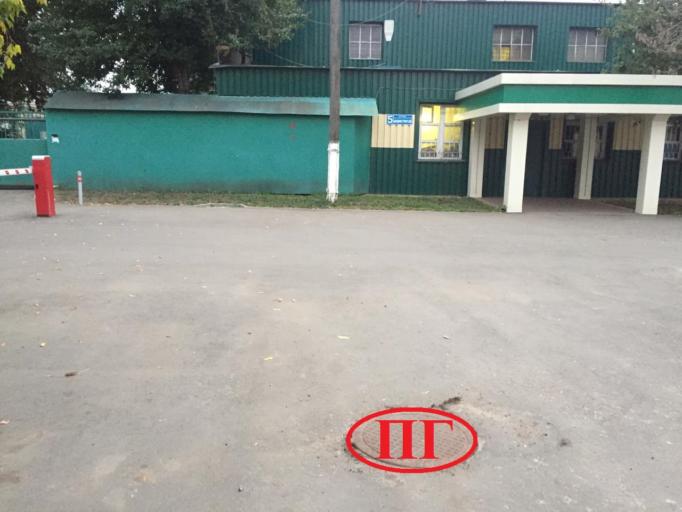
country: RU
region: Voronezj
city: Voronezh
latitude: 51.6816
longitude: 39.1675
